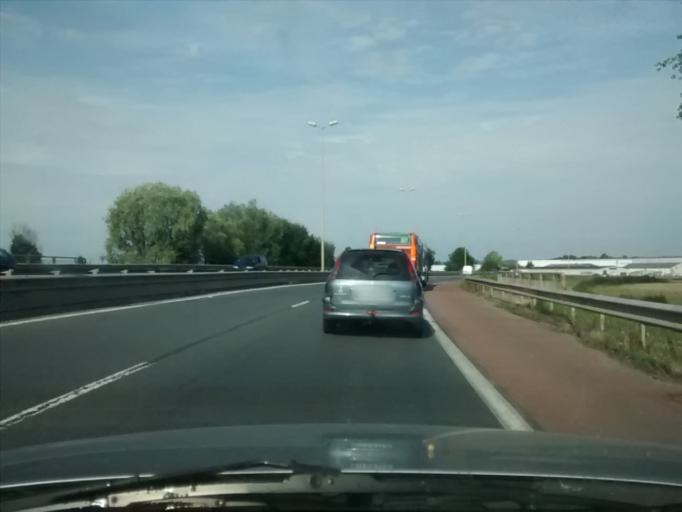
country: FR
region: Pays de la Loire
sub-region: Departement de la Sarthe
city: La Chapelle-Saint-Aubin
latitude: 48.0261
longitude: 0.1692
